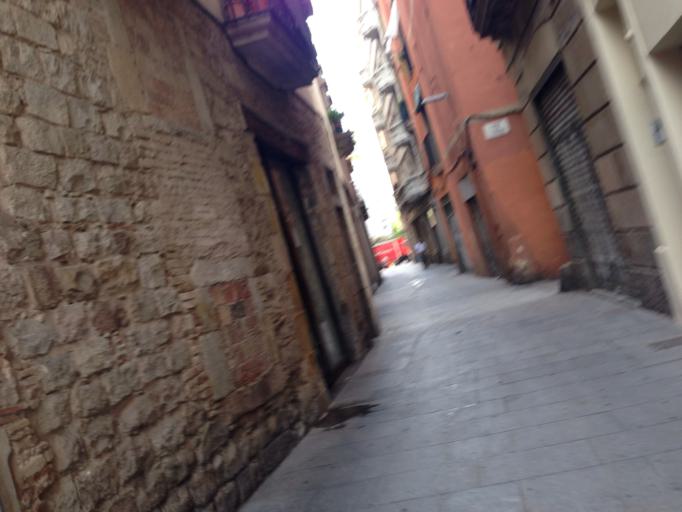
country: ES
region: Catalonia
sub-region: Provincia de Barcelona
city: Ciutat Vella
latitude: 41.3865
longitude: 2.1785
